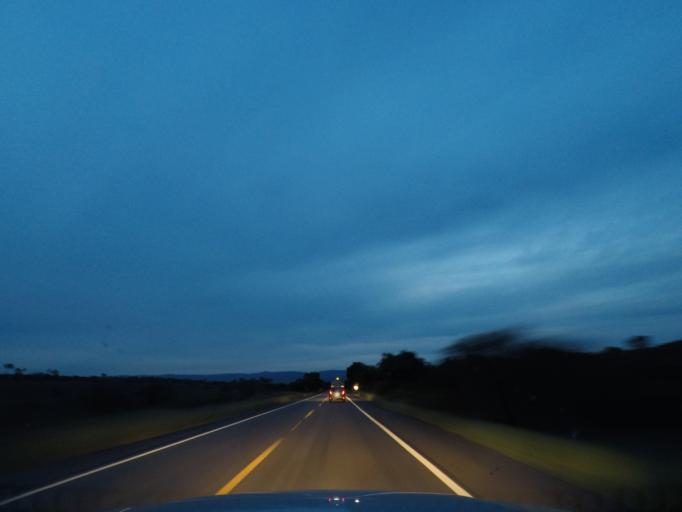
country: BR
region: Bahia
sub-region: Andarai
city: Vera Cruz
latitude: -12.4947
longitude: -41.3083
